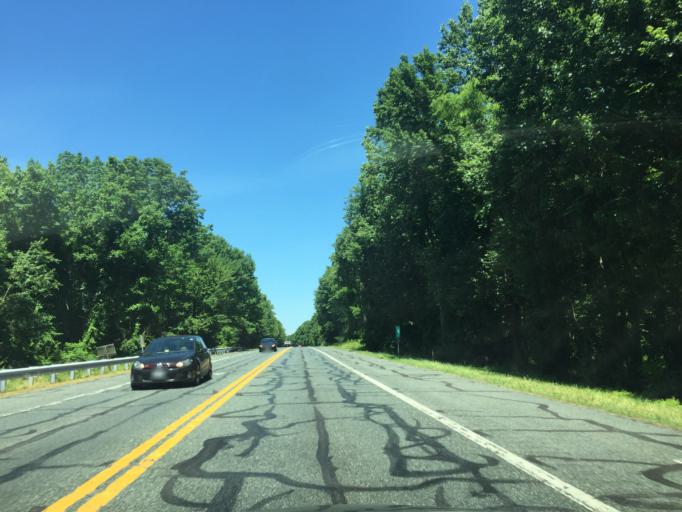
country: US
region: Maryland
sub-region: Harford County
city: Jarrettsville
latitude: 39.5803
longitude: -76.4483
